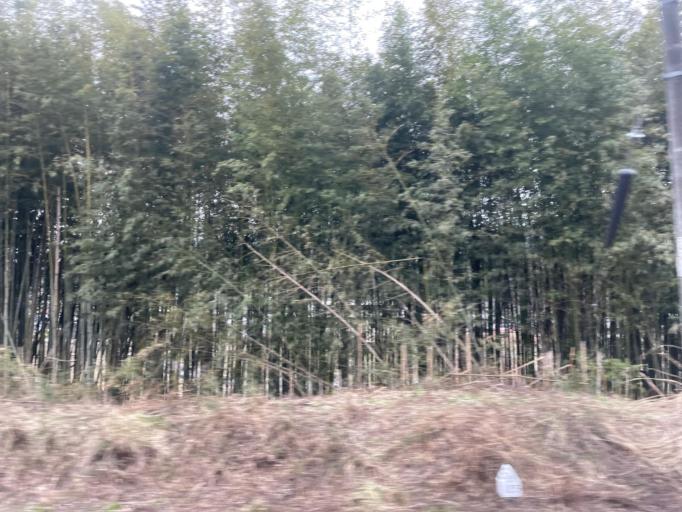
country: JP
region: Gunma
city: Numata
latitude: 36.6978
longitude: 138.9861
